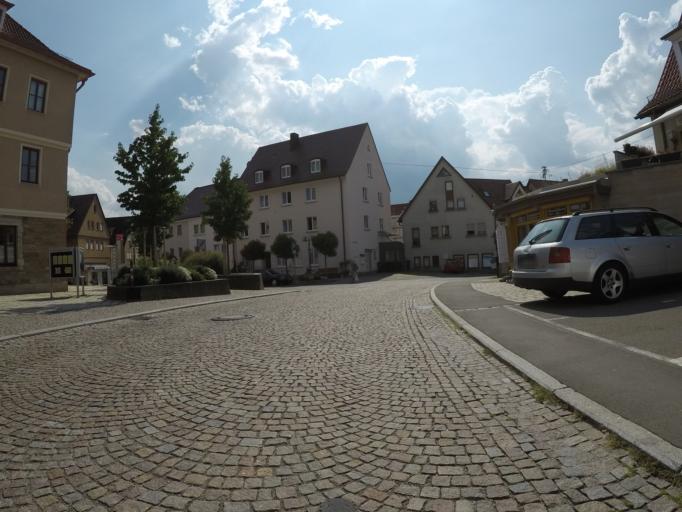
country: DE
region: Baden-Wuerttemberg
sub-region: Tuebingen Region
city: Eningen unter Achalm
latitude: 48.4866
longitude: 9.2581
